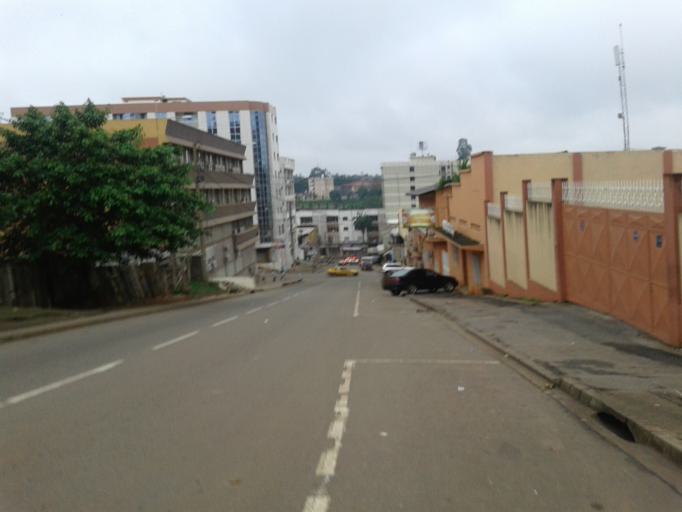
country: CM
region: Centre
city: Yaounde
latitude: 3.8709
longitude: 11.5170
